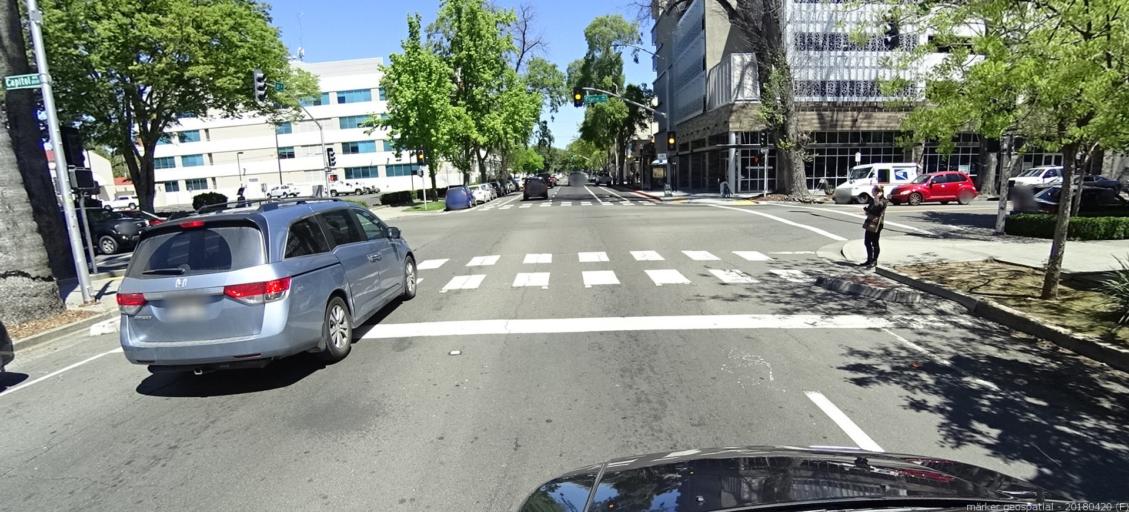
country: US
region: California
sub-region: Sacramento County
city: Sacramento
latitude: 38.5728
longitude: -121.4801
